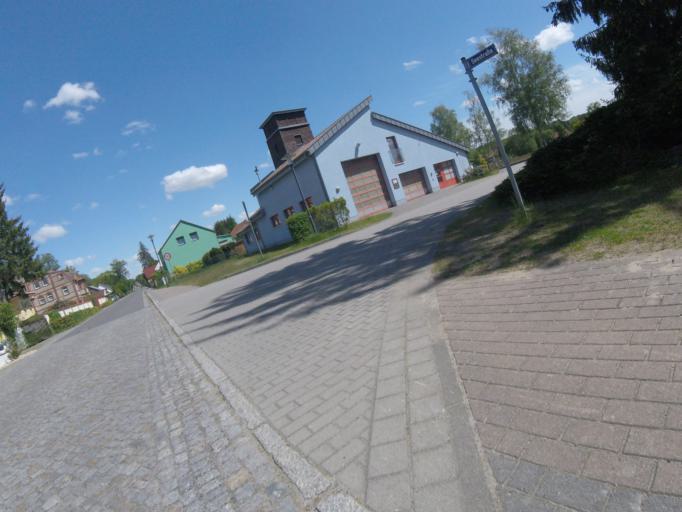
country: DE
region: Brandenburg
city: Schwerin
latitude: 52.1530
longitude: 13.6370
